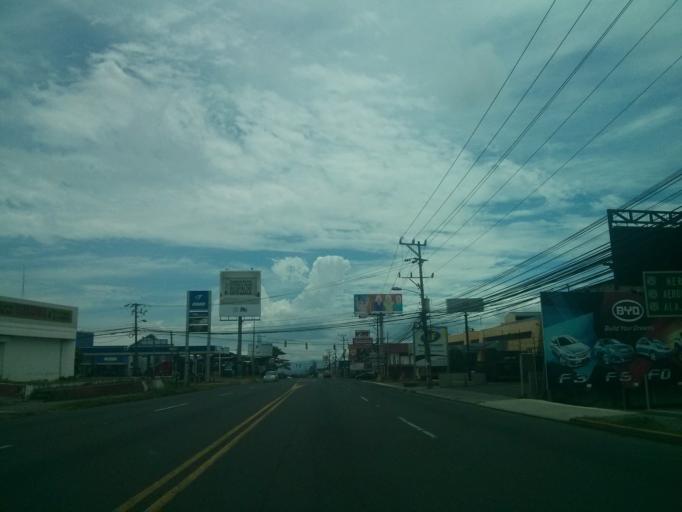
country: CR
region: San Jose
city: Colima
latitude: 9.9513
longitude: -84.1047
